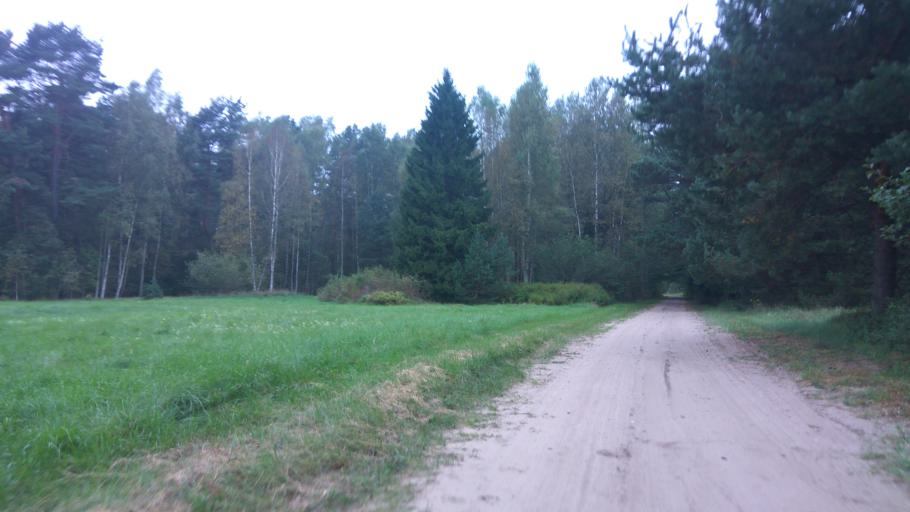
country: LV
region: Rucavas
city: Rucava
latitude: 56.1750
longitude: 21.1638
